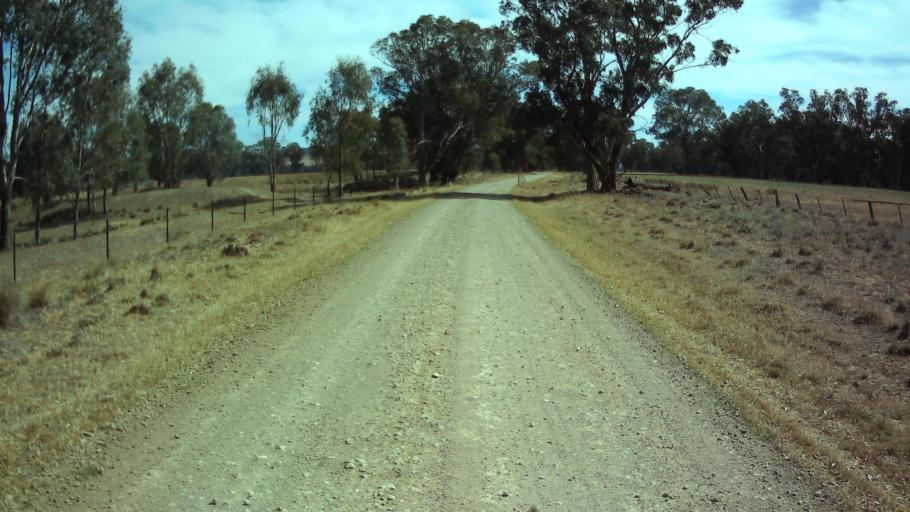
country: AU
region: New South Wales
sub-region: Weddin
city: Grenfell
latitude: -33.6916
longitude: 148.3039
